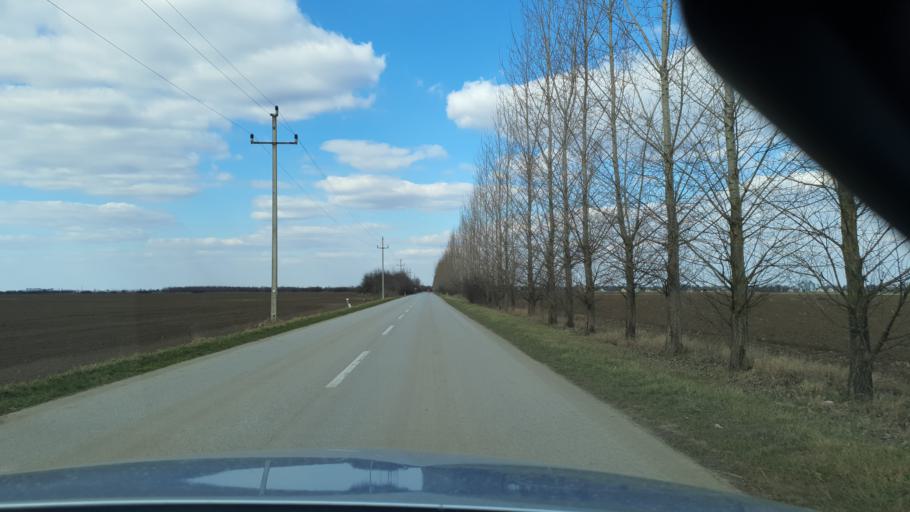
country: RS
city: Ravno Selo
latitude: 45.4349
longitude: 19.6061
